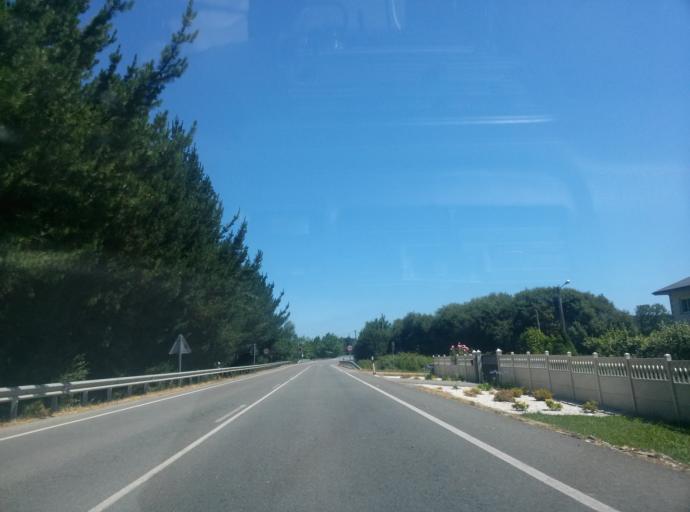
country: ES
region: Galicia
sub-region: Provincia de Lugo
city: Castro de Rei
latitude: 43.2484
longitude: -7.4160
